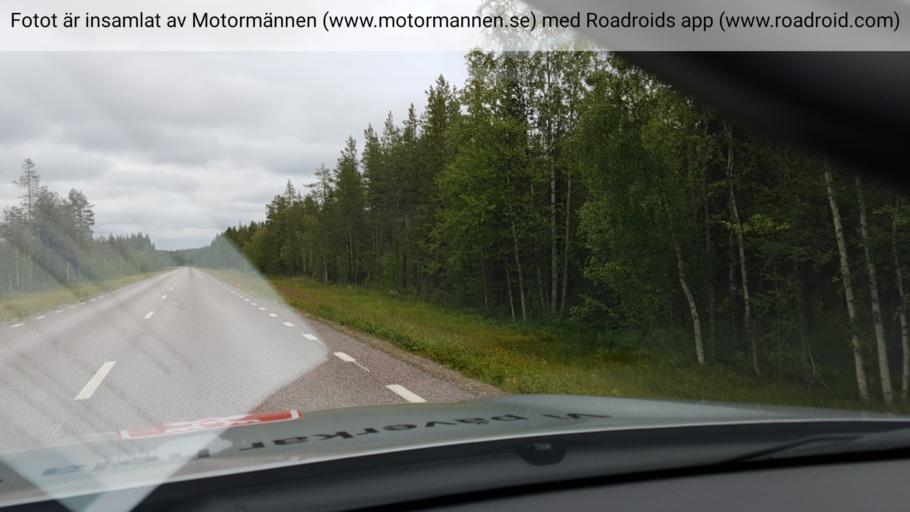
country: SE
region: Norrbotten
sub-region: Gallivare Kommun
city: Gaellivare
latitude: 67.0573
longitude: 21.2505
